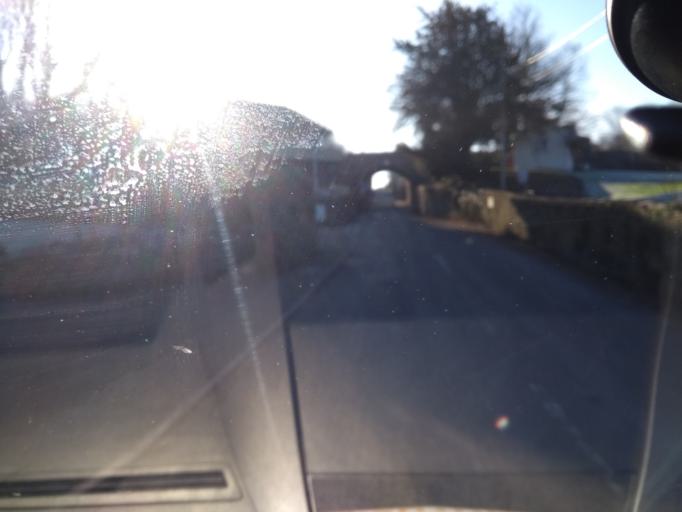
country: GB
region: England
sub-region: Somerset
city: Bruton
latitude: 51.1115
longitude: -2.4503
